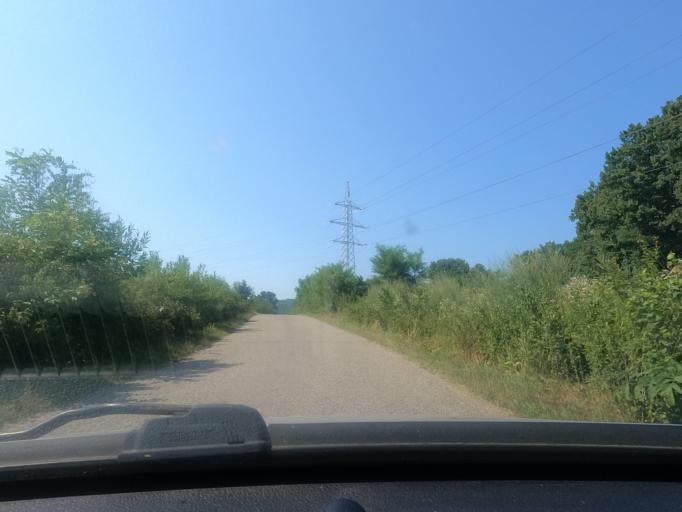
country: RS
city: Jarebice
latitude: 44.5393
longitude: 19.3707
